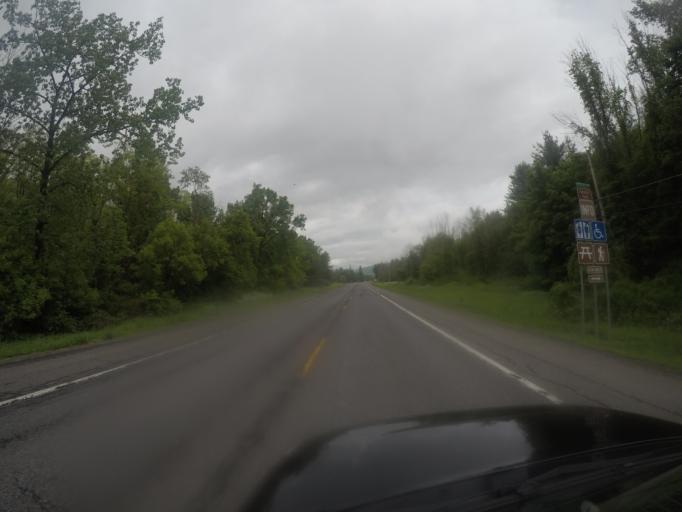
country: US
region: New York
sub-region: Ulster County
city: Shokan
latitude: 42.0258
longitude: -74.2714
